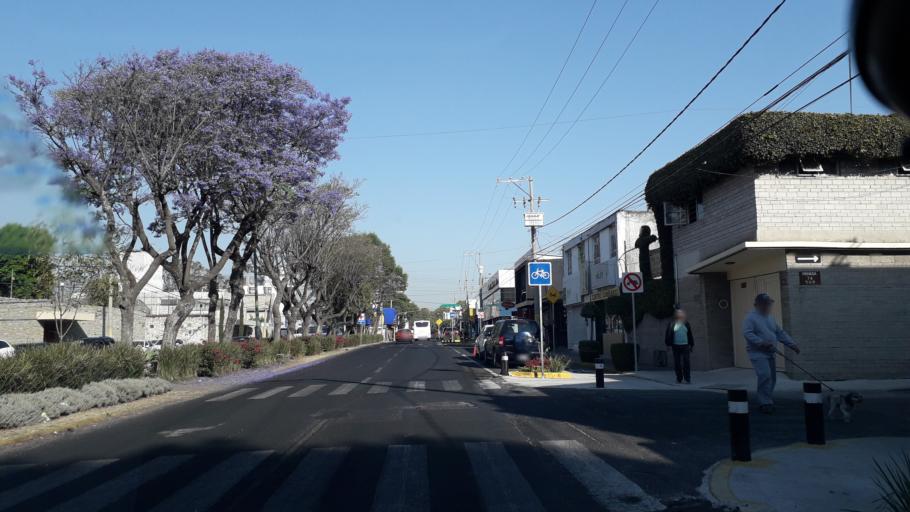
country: MX
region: Puebla
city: Puebla
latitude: 19.0305
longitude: -98.2133
